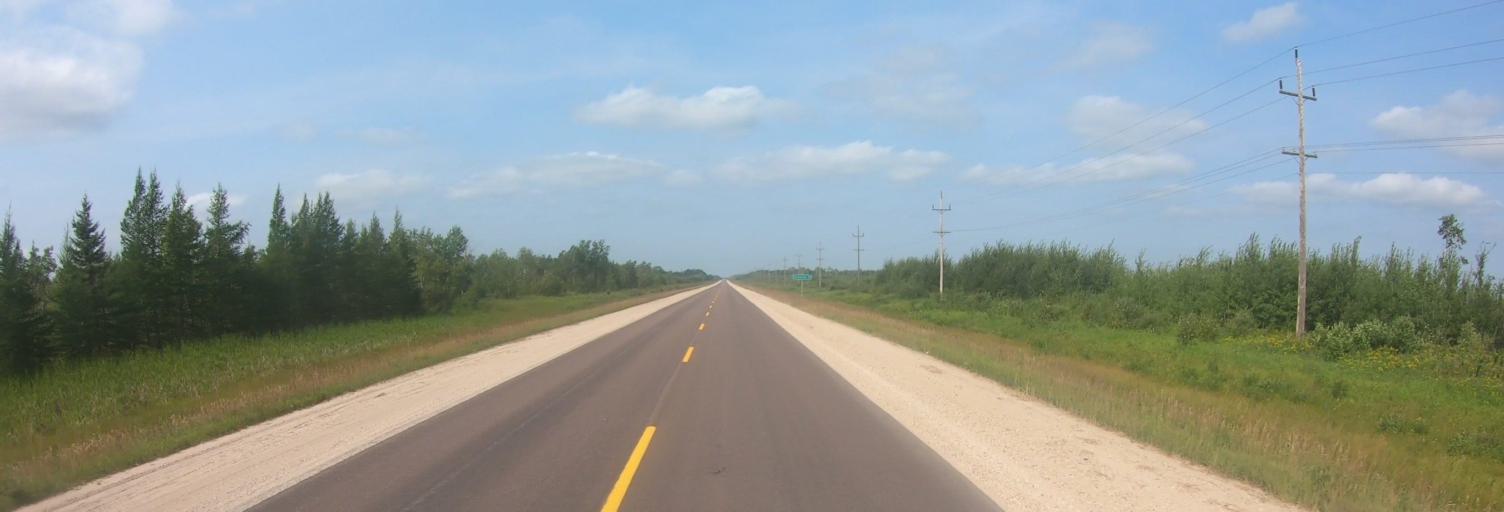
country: CA
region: Manitoba
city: La Broquerie
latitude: 49.2671
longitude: -96.3755
